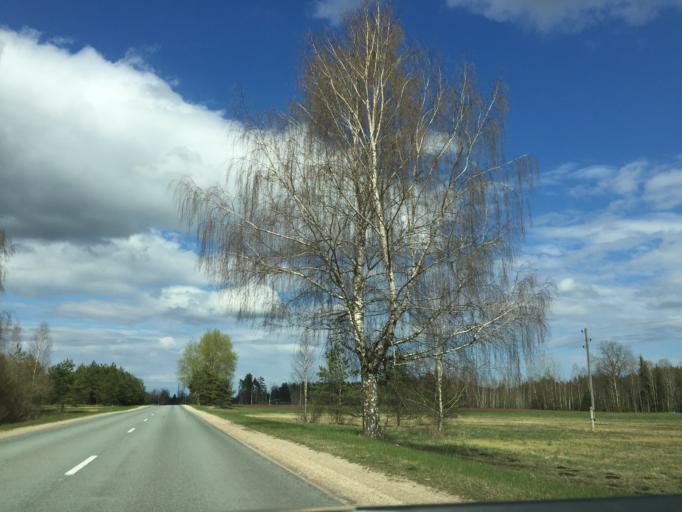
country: LV
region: Gulbenes Rajons
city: Gulbene
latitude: 57.2672
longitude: 26.5646
